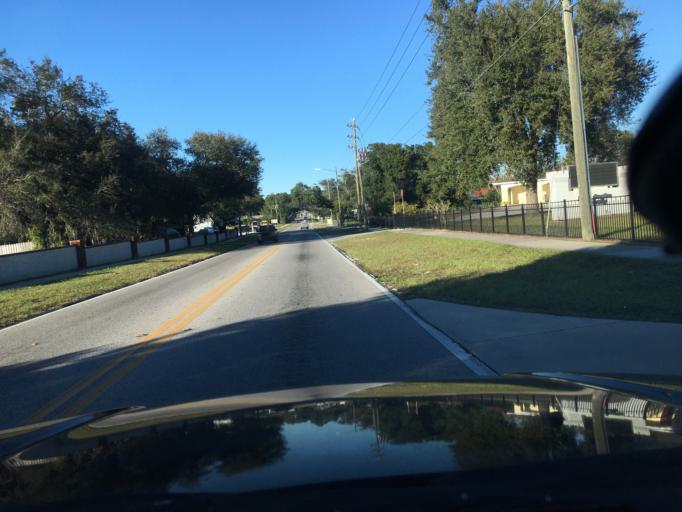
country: US
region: Florida
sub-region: Orange County
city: Lockhart
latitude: 28.5952
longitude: -81.4679
